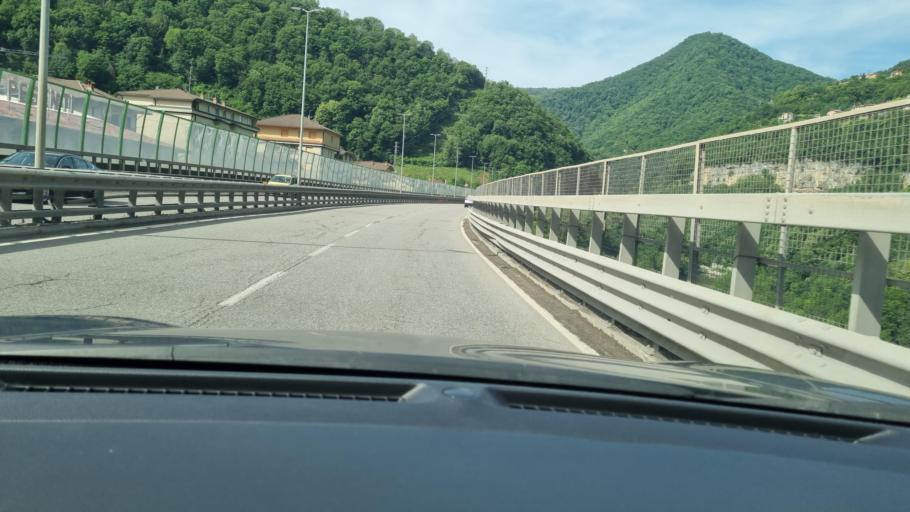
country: IT
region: Lombardy
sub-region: Provincia di Bergamo
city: Sedrina
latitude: 45.7818
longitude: 9.6219
